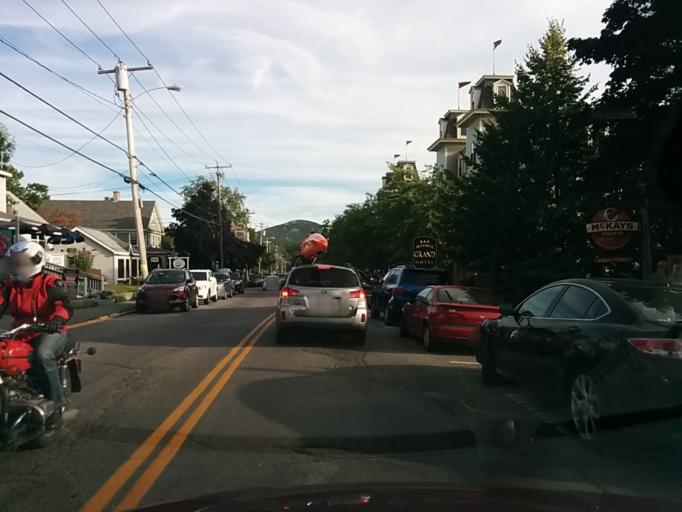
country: US
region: Maine
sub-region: Hancock County
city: Bar Harbor
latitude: 44.3862
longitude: -68.2040
